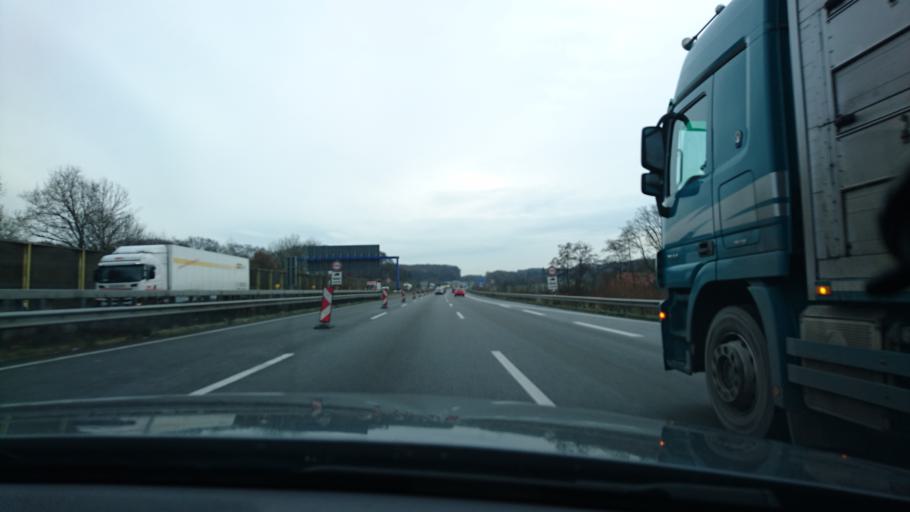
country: DE
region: North Rhine-Westphalia
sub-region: Regierungsbezirk Munster
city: Lotte
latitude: 52.3072
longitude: 7.9468
